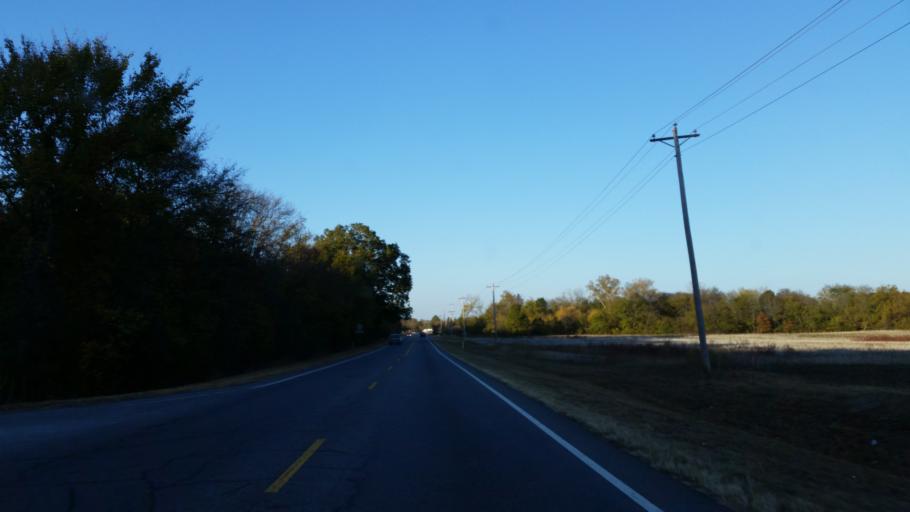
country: US
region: Georgia
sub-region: Bartow County
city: Adairsville
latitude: 34.4169
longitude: -84.9356
